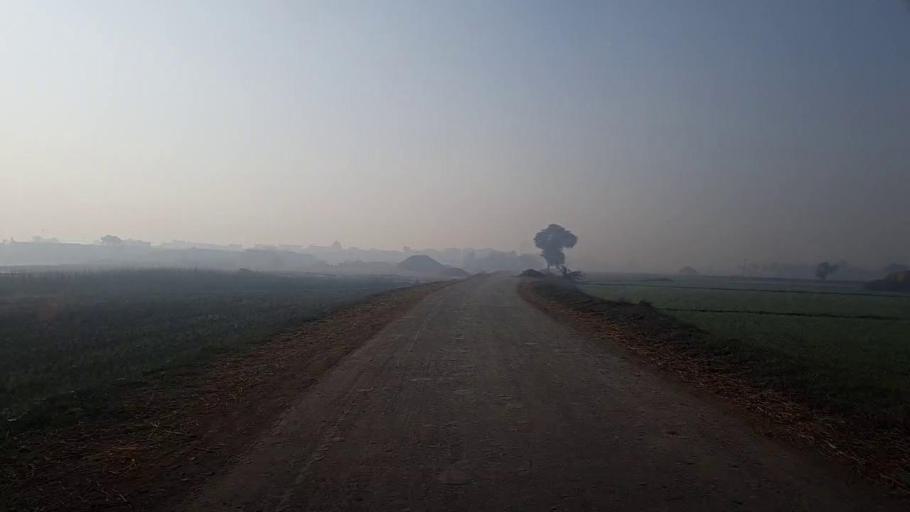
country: PK
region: Sindh
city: Mehar
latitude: 27.1395
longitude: 67.8233
